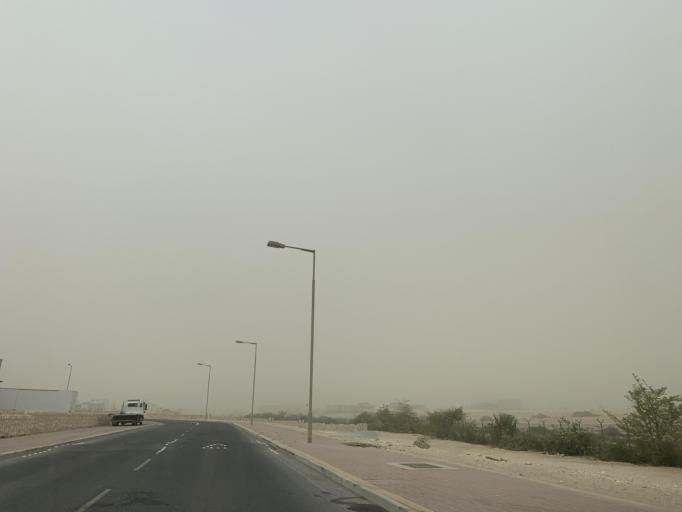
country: BH
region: Central Governorate
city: Madinat Hamad
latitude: 26.1289
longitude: 50.5145
